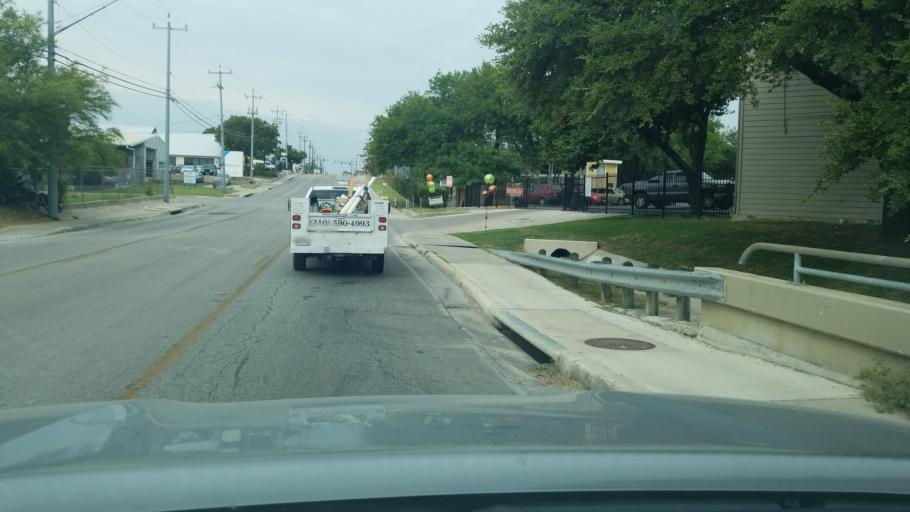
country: US
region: Texas
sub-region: Bexar County
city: Castle Hills
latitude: 29.5304
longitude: -98.4909
